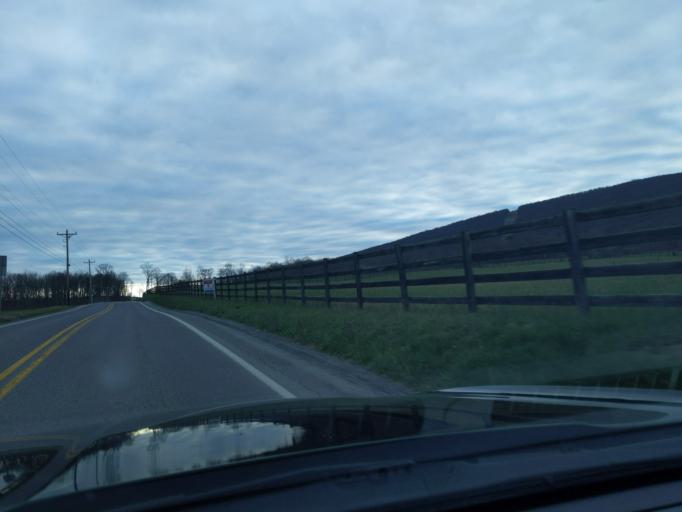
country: US
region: Pennsylvania
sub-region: Blair County
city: Lakemont
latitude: 40.4739
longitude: -78.3273
